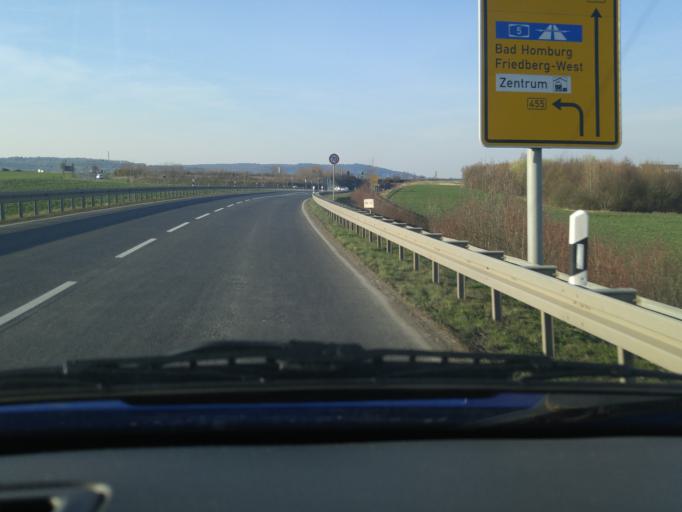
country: DE
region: Hesse
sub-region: Regierungsbezirk Darmstadt
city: Friedberg
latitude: 50.3200
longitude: 8.7356
